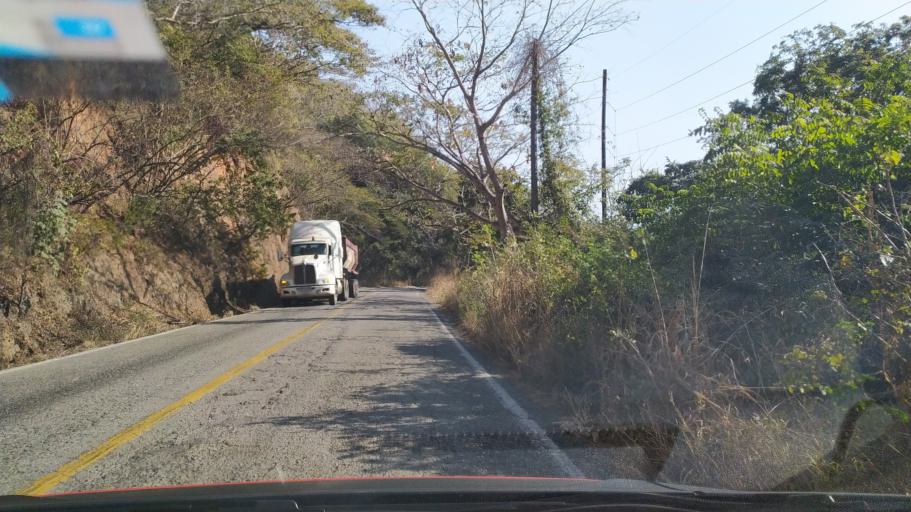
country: MX
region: Michoacan
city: Coahuayana Viejo
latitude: 18.6008
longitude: -103.6795
